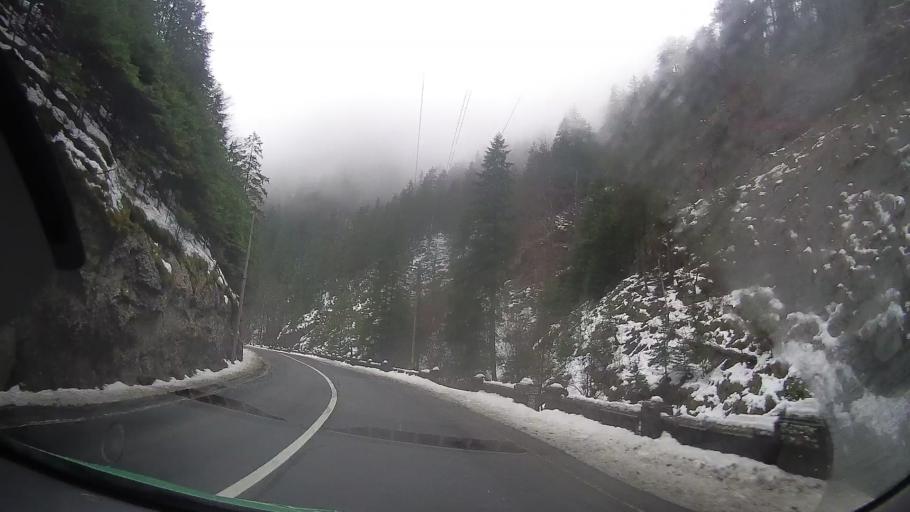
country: RO
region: Neamt
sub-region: Comuna Bicaz Chei
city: Bicaz Chei
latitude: 46.8018
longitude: 25.8016
